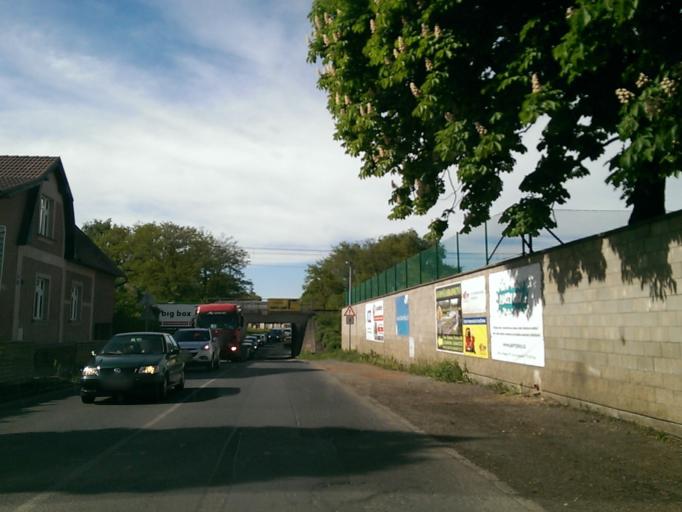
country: CZ
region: Praha
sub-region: Praha 20
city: Horni Pocernice
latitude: 50.1185
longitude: 14.6253
